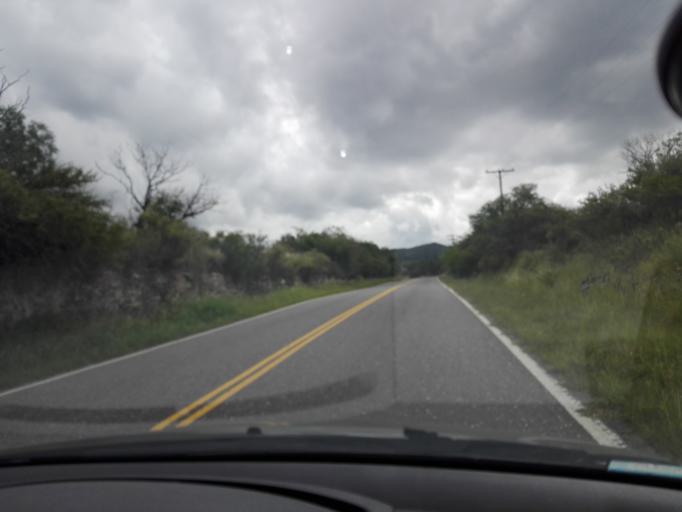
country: AR
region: Cordoba
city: Alta Gracia
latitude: -31.5944
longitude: -64.4867
